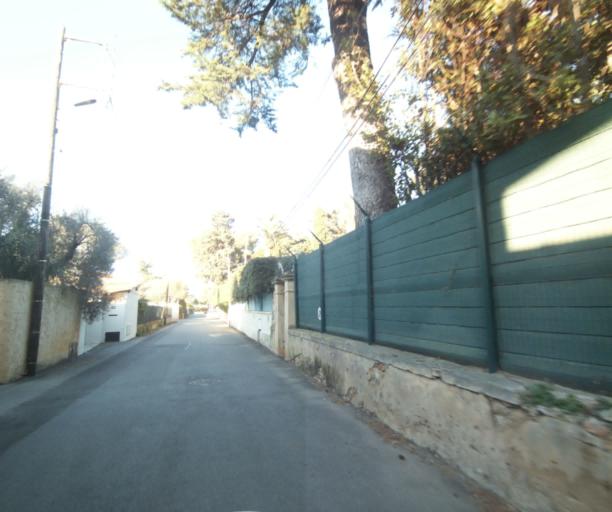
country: FR
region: Provence-Alpes-Cote d'Azur
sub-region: Departement des Alpes-Maritimes
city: Antibes
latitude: 43.5495
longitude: 7.1267
